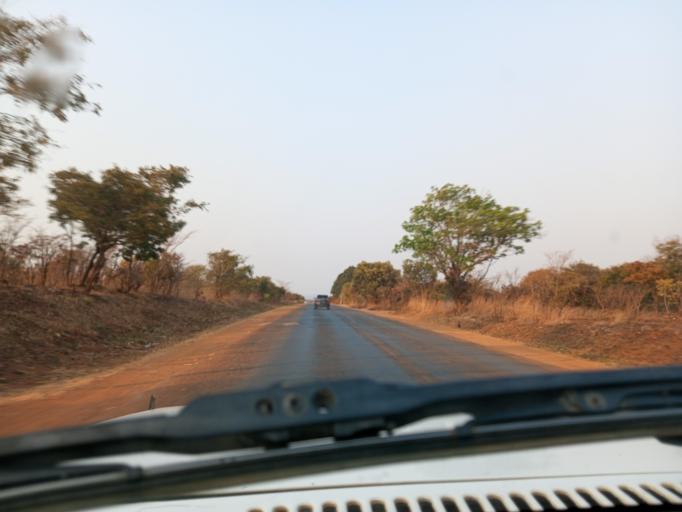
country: ZM
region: Northern
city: Mpika
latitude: -11.8894
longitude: 31.4200
